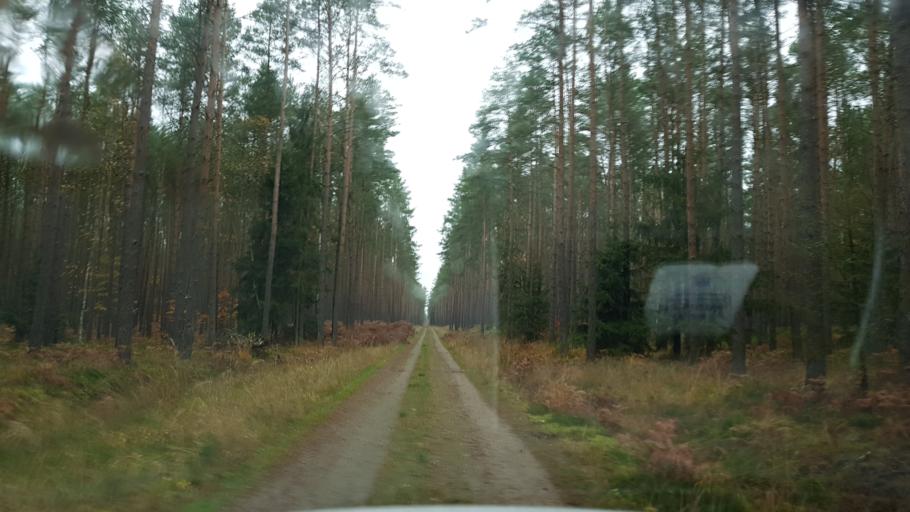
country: PL
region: West Pomeranian Voivodeship
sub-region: Powiat goleniowski
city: Stepnica
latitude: 53.6364
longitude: 14.7117
